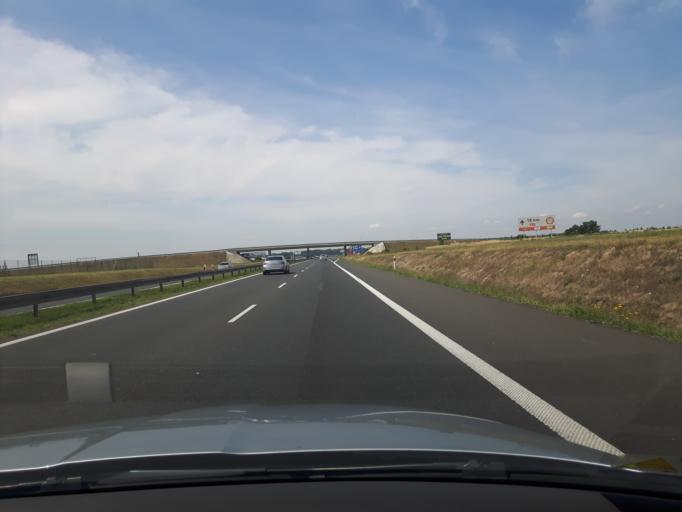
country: PL
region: Masovian Voivodeship
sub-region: Powiat nowodworski
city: Zakroczym
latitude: 52.4445
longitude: 20.6166
